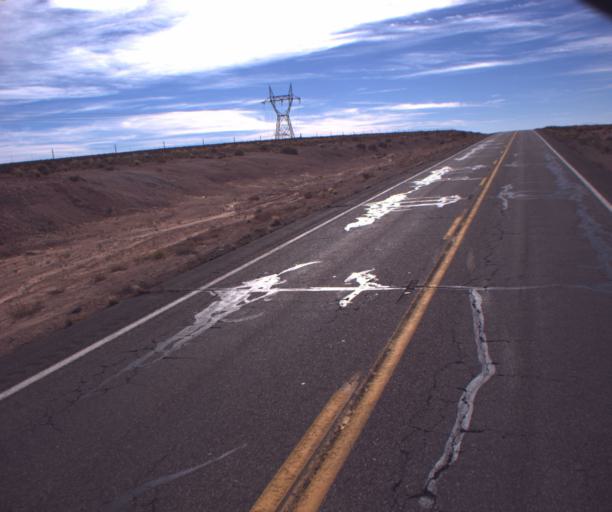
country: US
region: Arizona
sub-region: Coconino County
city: LeChee
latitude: 36.8002
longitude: -111.3025
